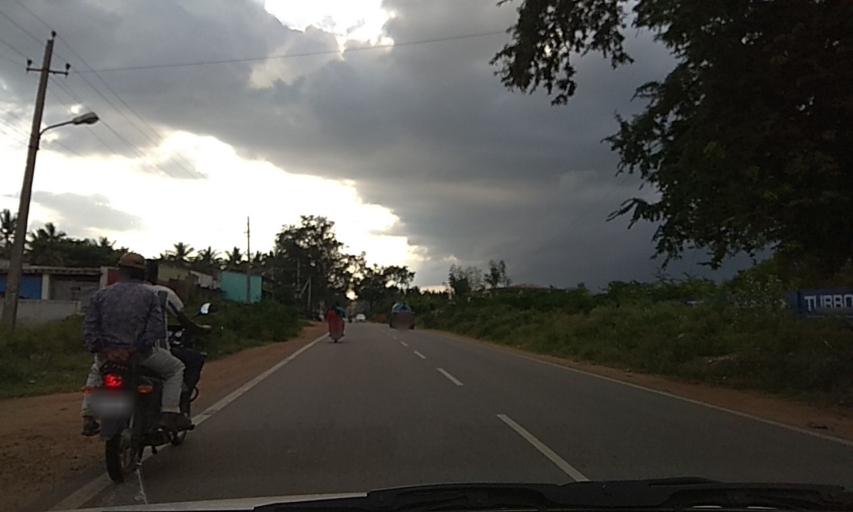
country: IN
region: Karnataka
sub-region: Chamrajnagar
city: Gundlupet
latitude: 11.8099
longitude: 76.6994
